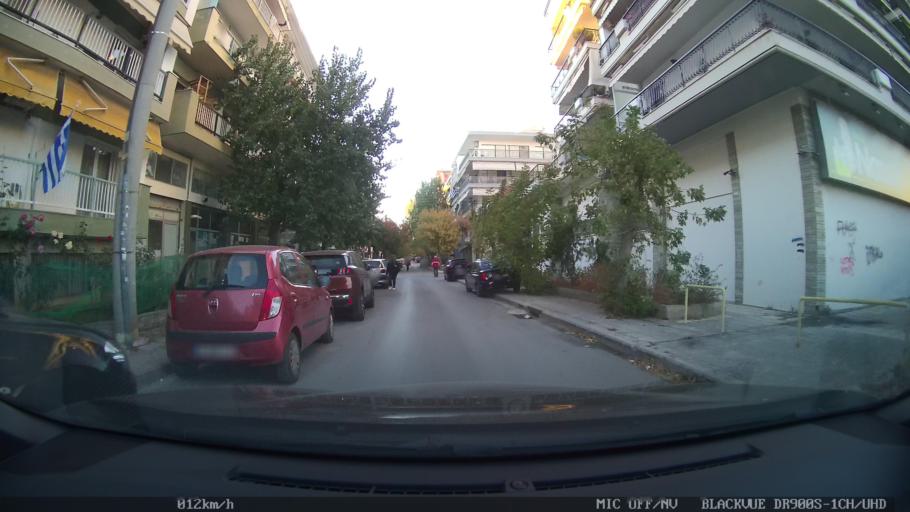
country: GR
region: Central Macedonia
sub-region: Nomos Thessalonikis
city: Pylaia
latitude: 40.6048
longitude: 22.9802
